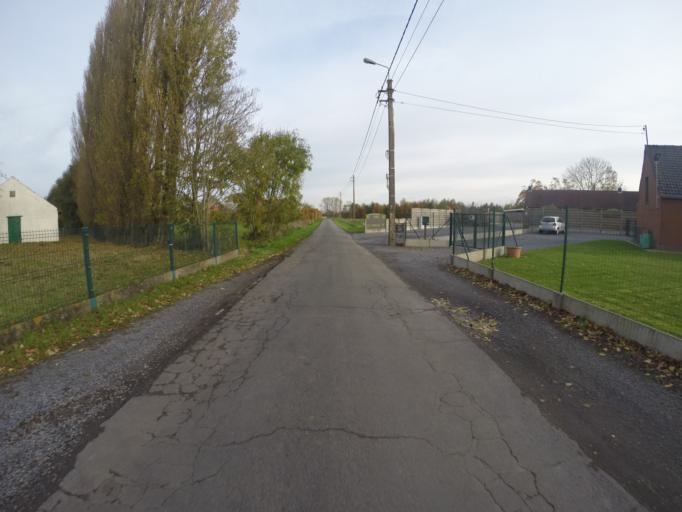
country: BE
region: Flanders
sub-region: Provincie Oost-Vlaanderen
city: Aalter
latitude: 51.0575
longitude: 3.4831
